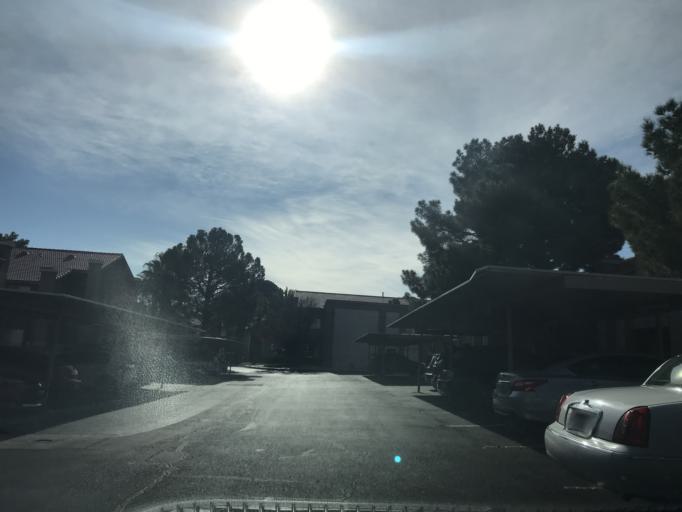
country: US
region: Nevada
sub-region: Clark County
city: Spring Valley
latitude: 36.0982
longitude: -115.2176
